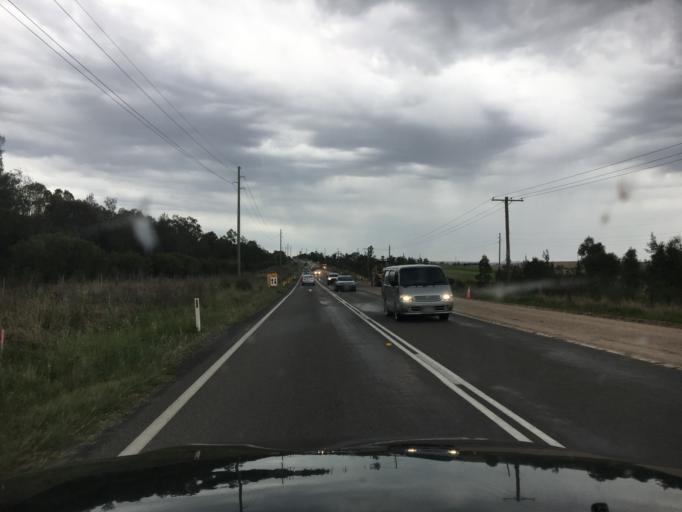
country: AU
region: New South Wales
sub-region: Muswellbrook
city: Muswellbrook
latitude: -32.1952
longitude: 150.8929
